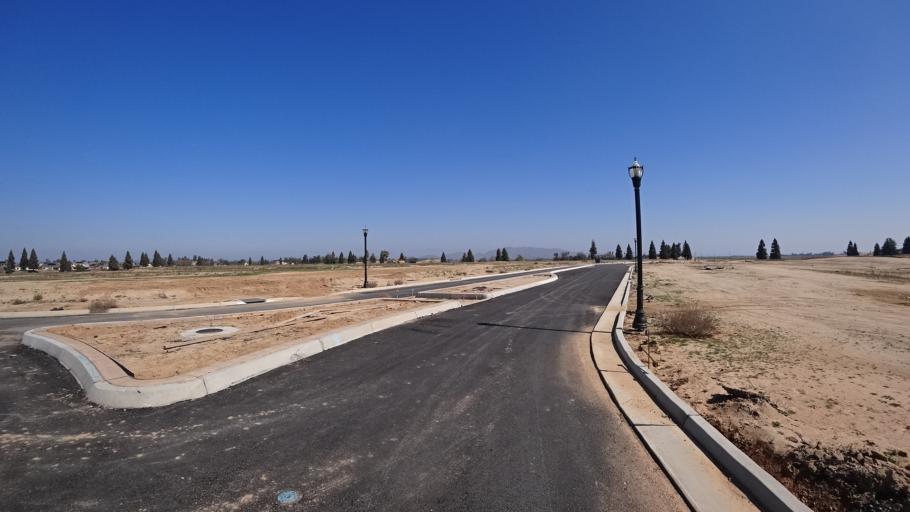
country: US
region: California
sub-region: Fresno County
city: Clovis
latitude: 36.9040
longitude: -119.7392
